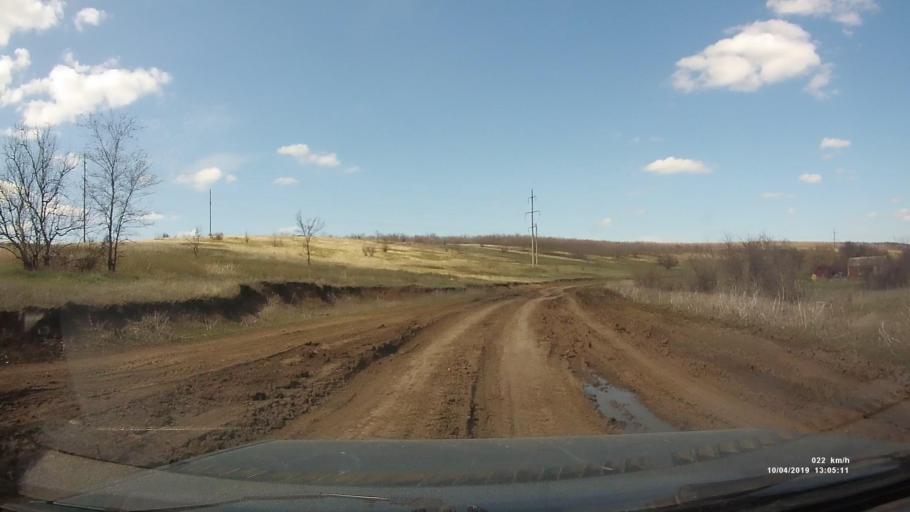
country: RU
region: Rostov
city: Masalovka
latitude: 48.3872
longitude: 40.2333
